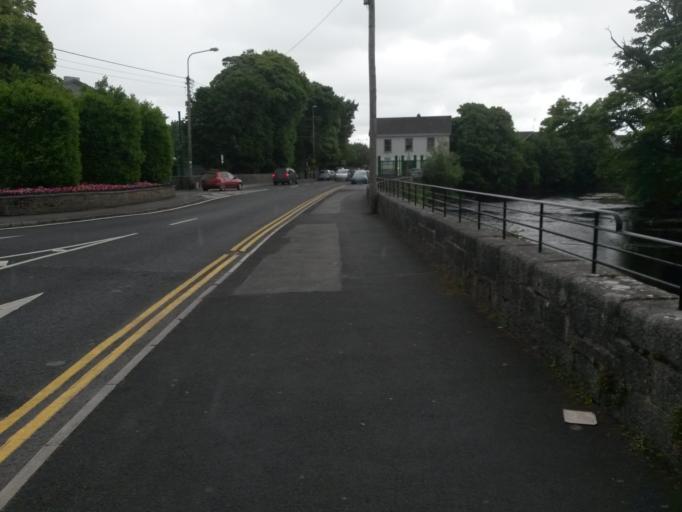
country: IE
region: Munster
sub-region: An Clar
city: Ennis
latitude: 52.8477
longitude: -8.9817
